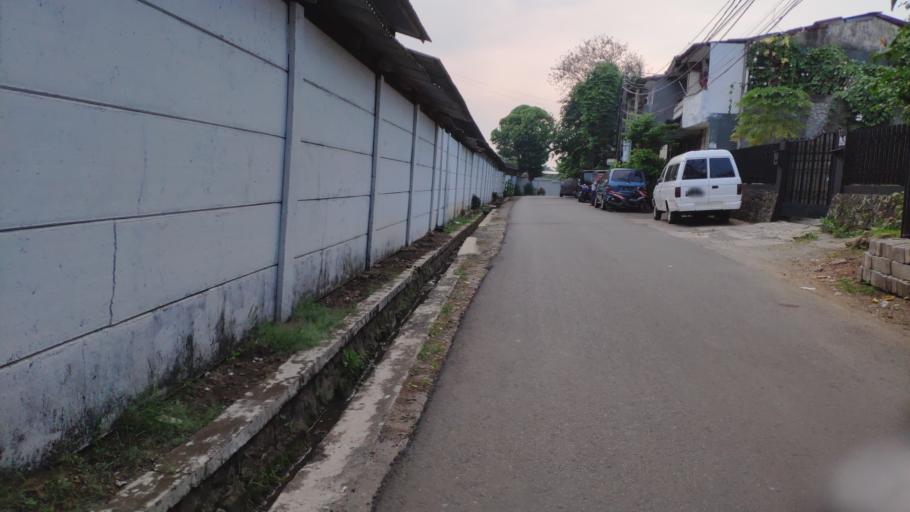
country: ID
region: West Java
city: Pamulang
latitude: -6.2984
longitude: 106.8113
